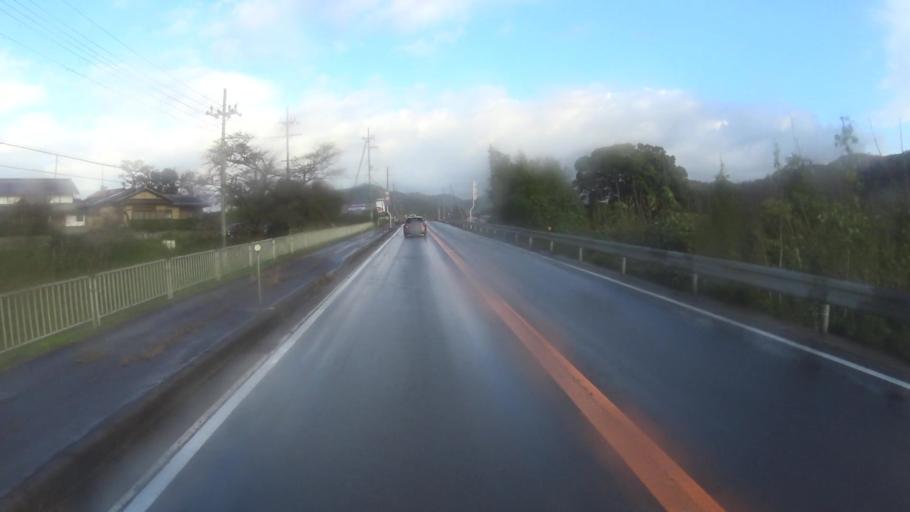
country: JP
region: Kyoto
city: Ayabe
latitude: 35.2445
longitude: 135.2166
